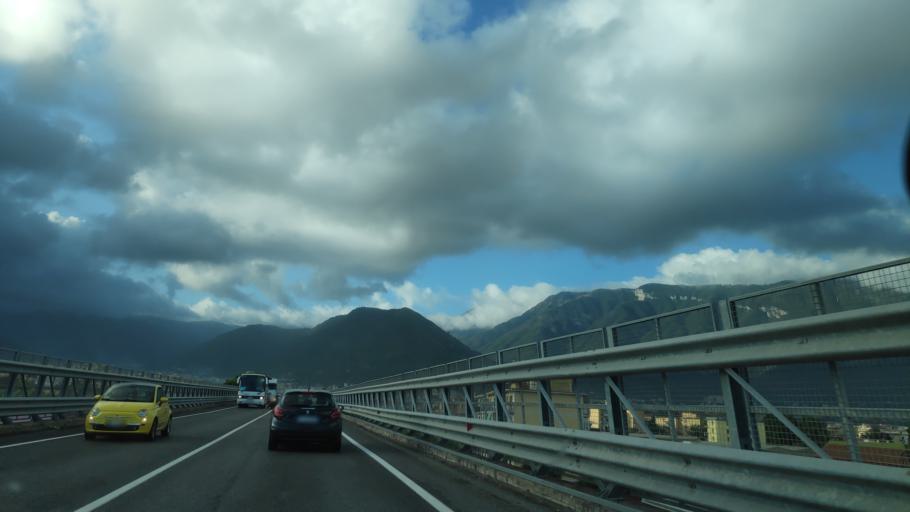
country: IT
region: Campania
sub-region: Provincia di Napoli
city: Castellammare di Stabia
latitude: 40.7148
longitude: 14.4958
